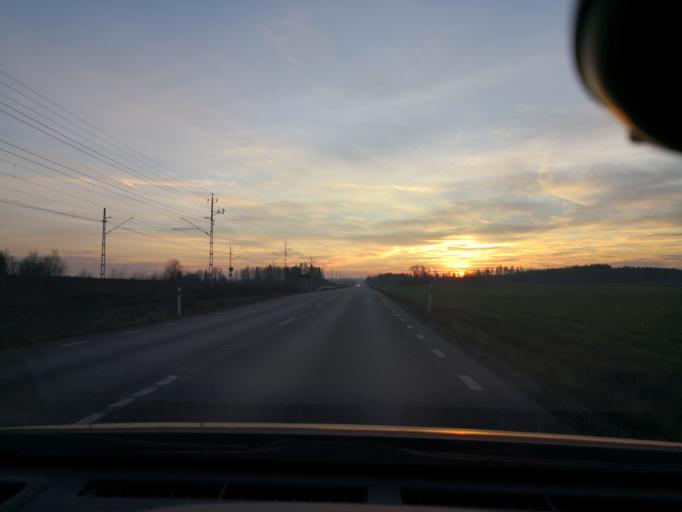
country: SE
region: Vaestmanland
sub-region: Kopings Kommun
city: Koping
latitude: 59.4329
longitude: 15.9354
